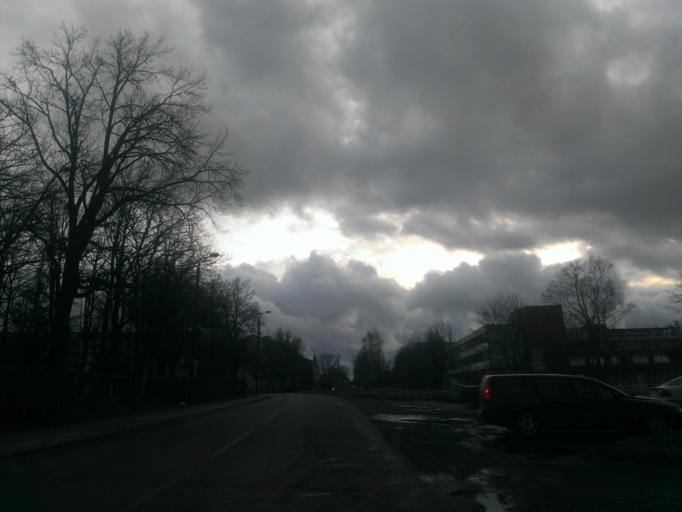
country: LV
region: Riga
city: Bolderaja
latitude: 57.0402
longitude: 24.0881
